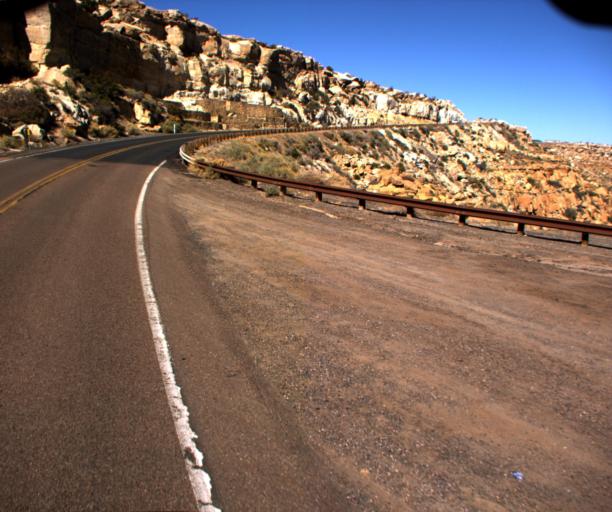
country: US
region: Arizona
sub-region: Navajo County
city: First Mesa
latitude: 35.8103
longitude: -110.5283
